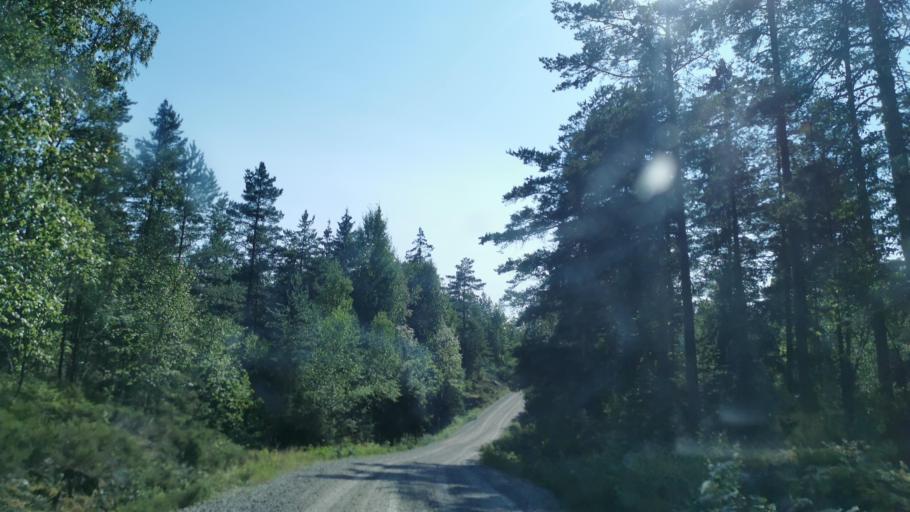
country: SE
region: OEstergoetland
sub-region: Norrkopings Kommun
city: Jursla
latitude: 58.7107
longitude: 16.1679
